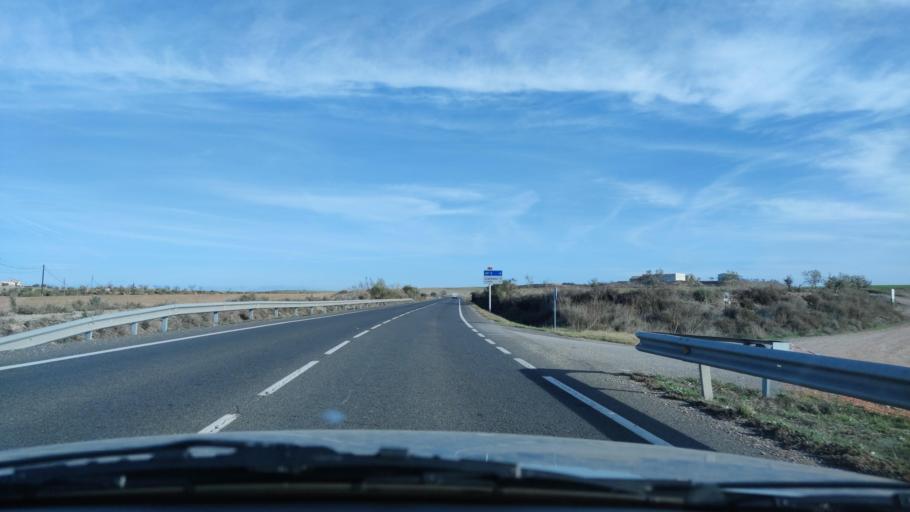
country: ES
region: Catalonia
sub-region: Provincia de Lleida
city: Alfes
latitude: 41.5274
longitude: 0.6298
